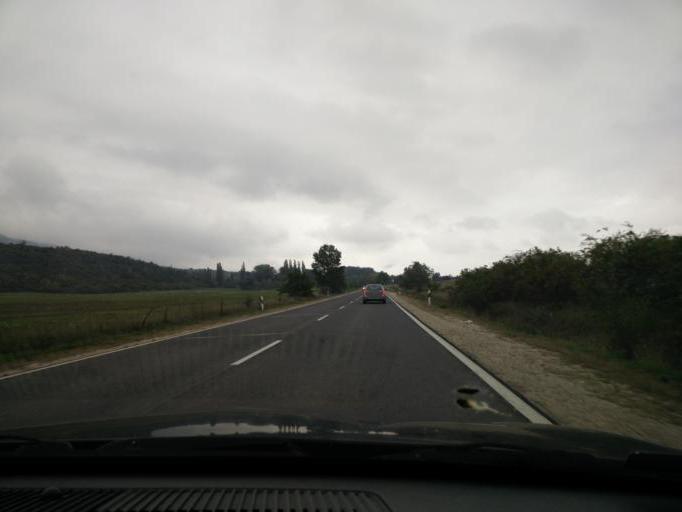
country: HU
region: Komarom-Esztergom
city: Dorog
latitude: 47.7230
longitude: 18.7680
